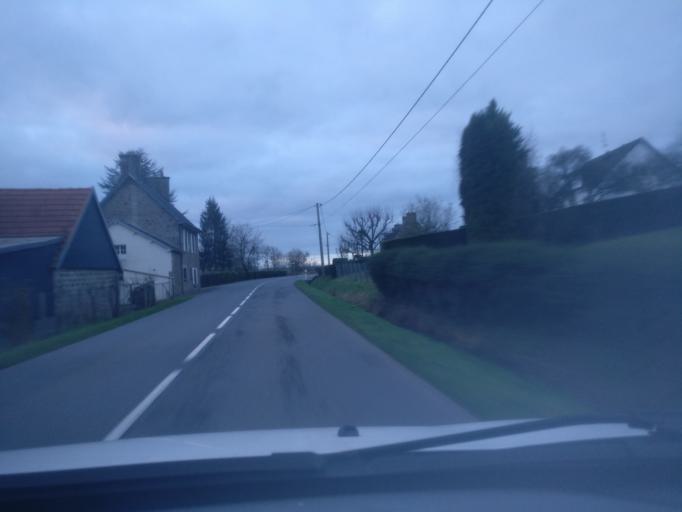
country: FR
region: Lower Normandy
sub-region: Departement de la Manche
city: Avranches
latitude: 48.6879
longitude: -1.3801
